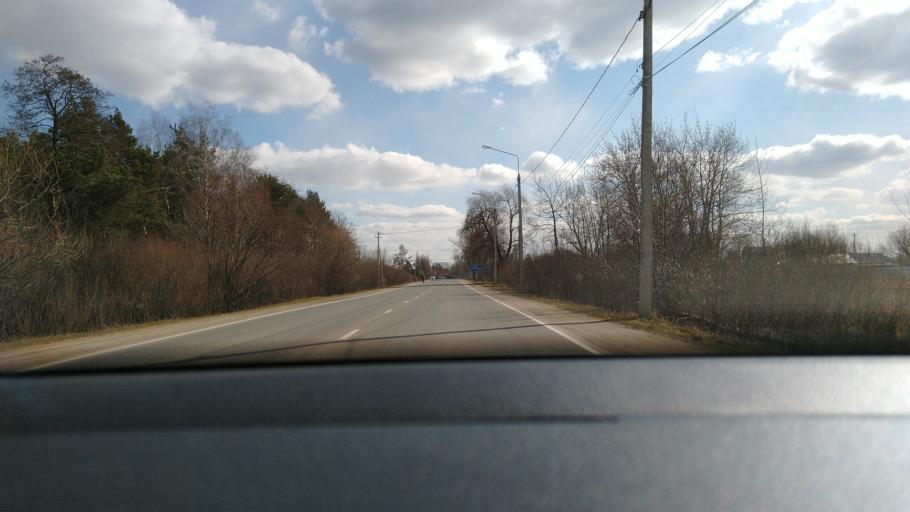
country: RU
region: Moskovskaya
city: Bol'shiye Vyazemy
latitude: 55.6231
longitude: 36.8687
